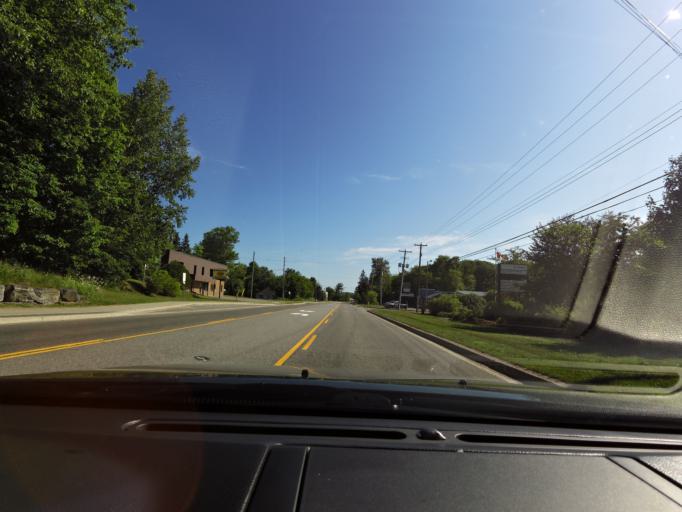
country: CA
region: Ontario
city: Huntsville
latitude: 45.3164
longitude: -79.2399
